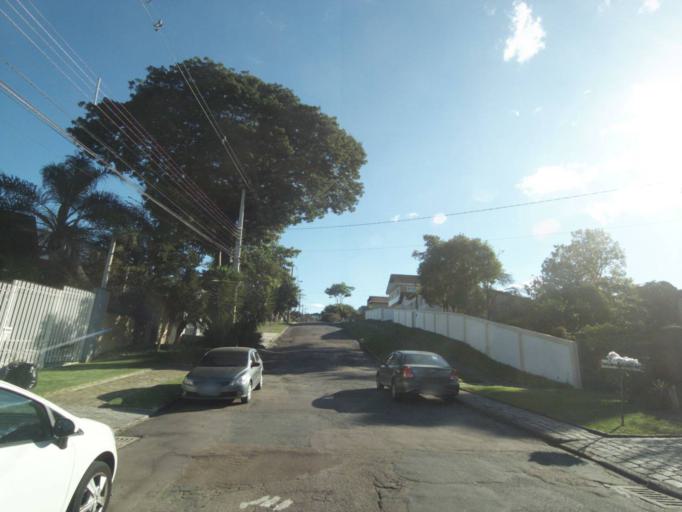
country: BR
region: Parana
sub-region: Curitiba
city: Curitiba
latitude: -25.3950
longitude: -49.2526
